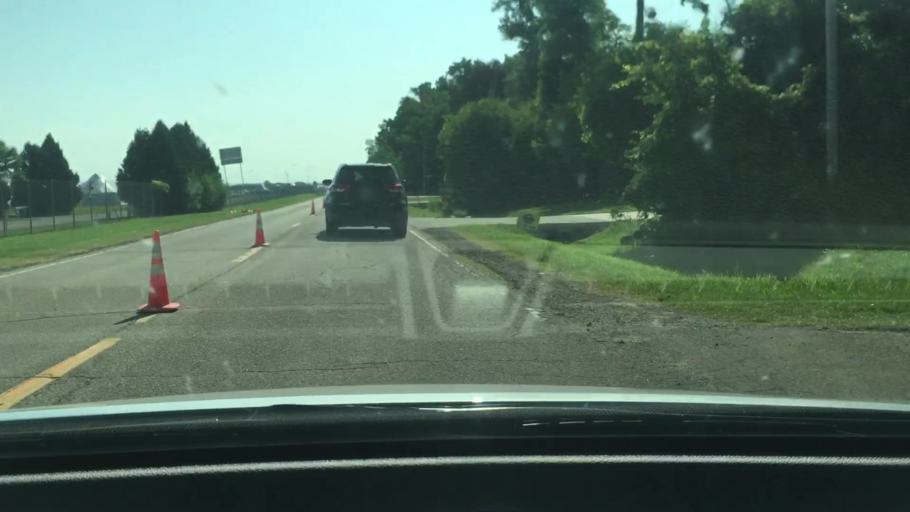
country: US
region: Wisconsin
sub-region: Winnebago County
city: Oshkosh
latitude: 43.9890
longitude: -88.5751
